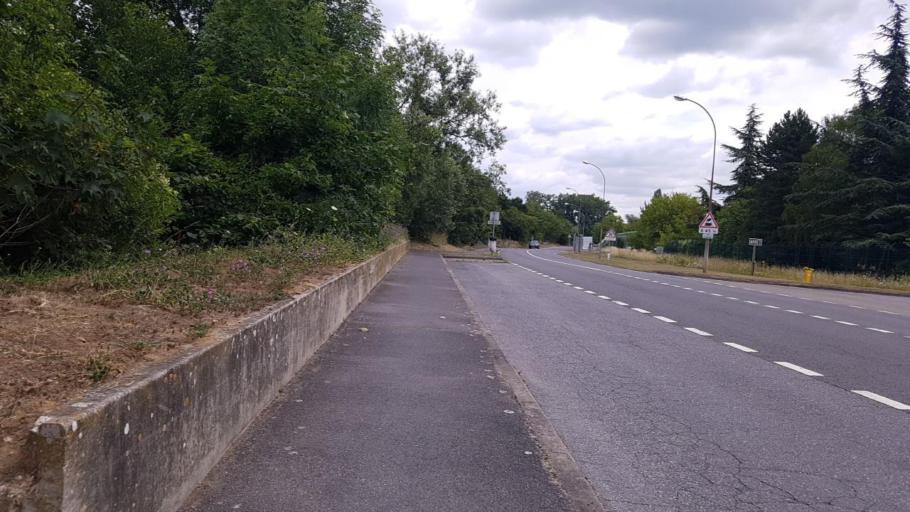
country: FR
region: Picardie
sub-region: Departement de l'Oise
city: Clairoix
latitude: 49.4330
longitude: 2.8439
